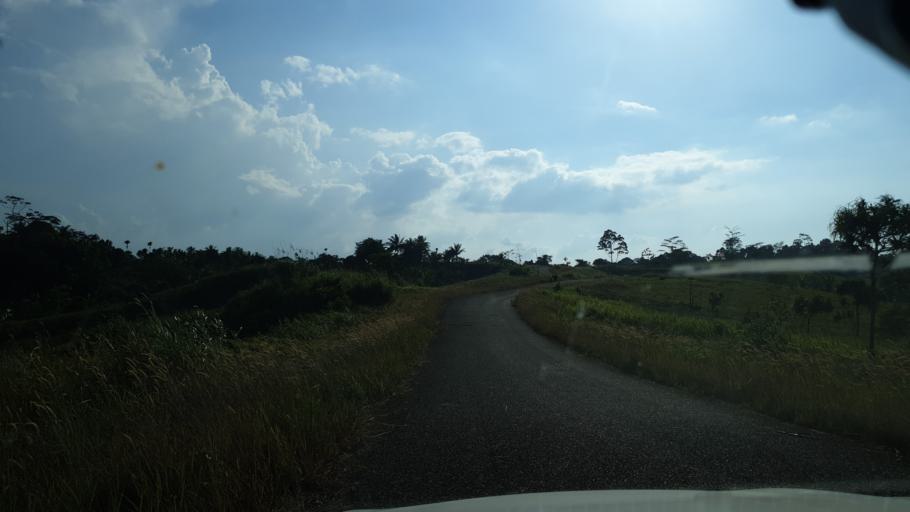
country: PG
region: East Sepik
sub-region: Wewak
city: Wewak
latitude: -3.7021
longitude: 143.7168
